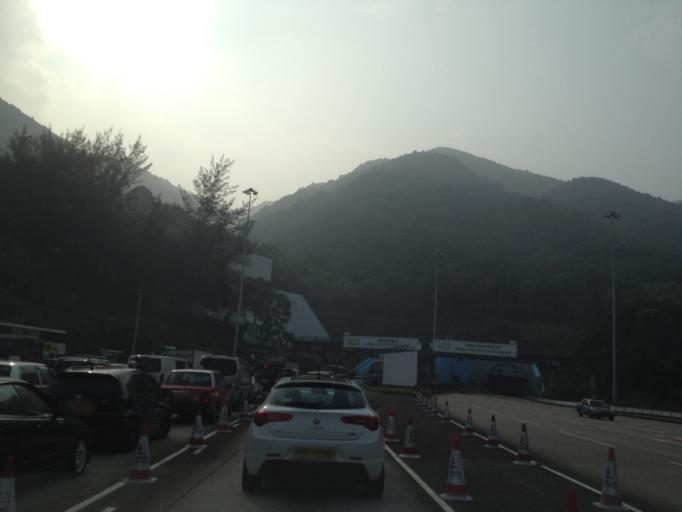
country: HK
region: Sha Tin
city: Sha Tin
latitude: 22.3773
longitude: 114.2120
